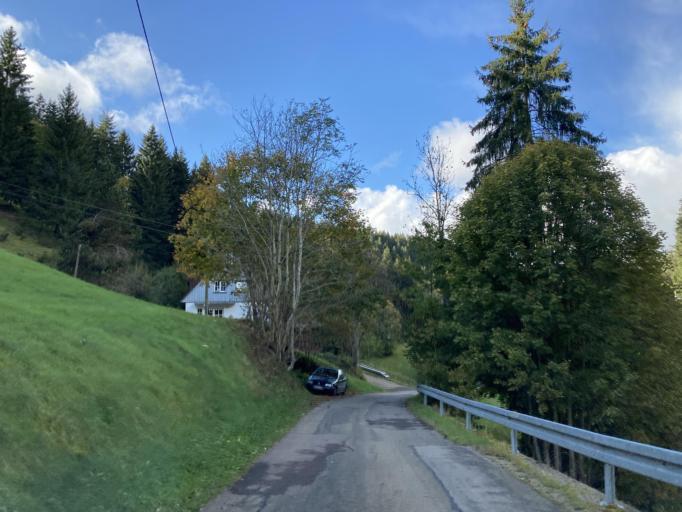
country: DE
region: Baden-Wuerttemberg
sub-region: Freiburg Region
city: Triberg im Schwarzwald
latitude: 48.1180
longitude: 8.2656
